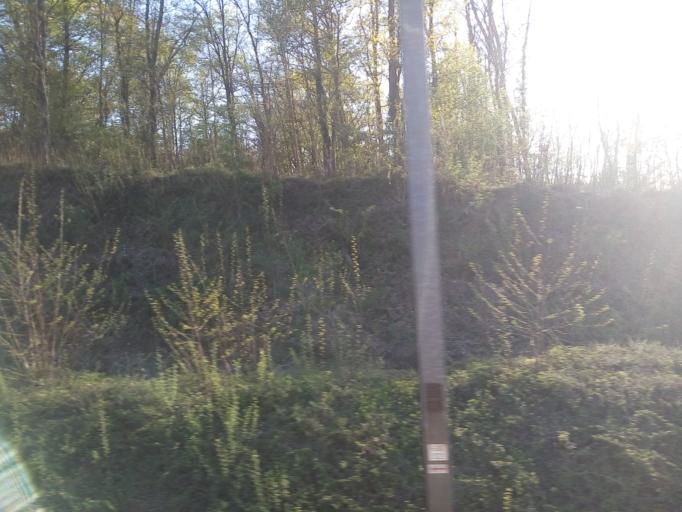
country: FR
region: Rhone-Alpes
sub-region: Departement de l'Isere
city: Saint-Didier-de-la-Tour
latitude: 45.5600
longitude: 5.4970
